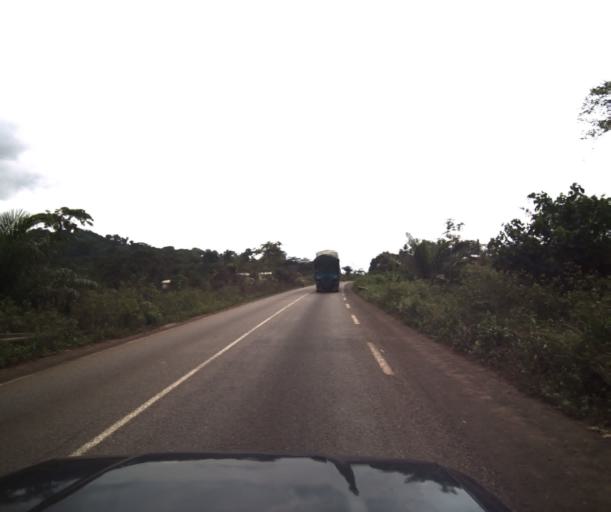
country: CM
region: Littoral
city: Edea
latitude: 3.8166
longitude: 10.3613
